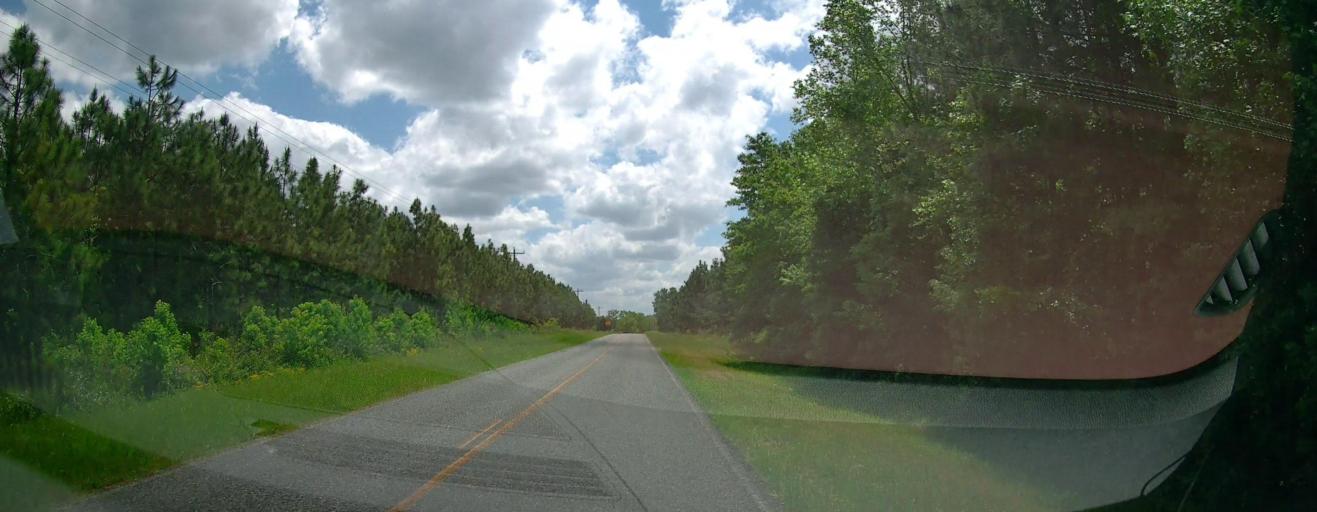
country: US
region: Georgia
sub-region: Dodge County
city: Chester
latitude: 32.5400
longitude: -83.1312
